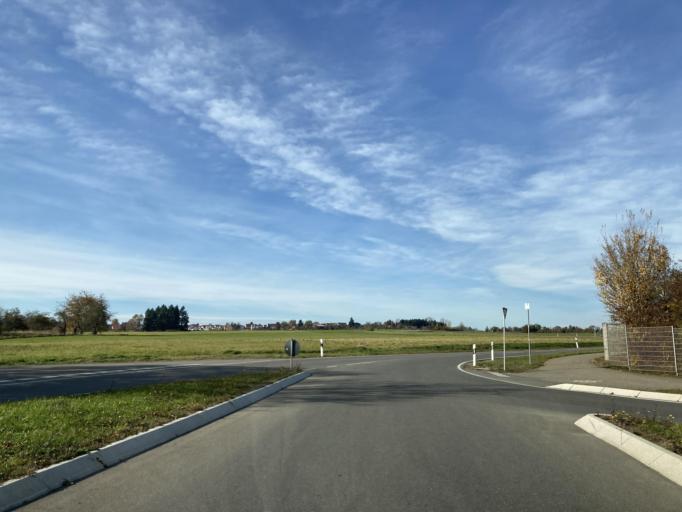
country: DE
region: Baden-Wuerttemberg
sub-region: Tuebingen Region
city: Bodelshausen
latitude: 48.3815
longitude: 8.9594
